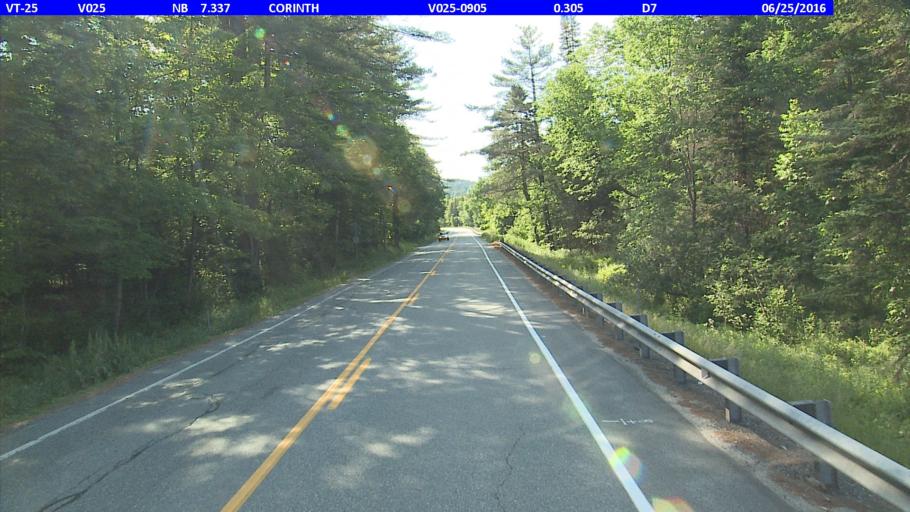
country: US
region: New Hampshire
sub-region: Grafton County
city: Haverhill
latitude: 44.0442
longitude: -72.2083
